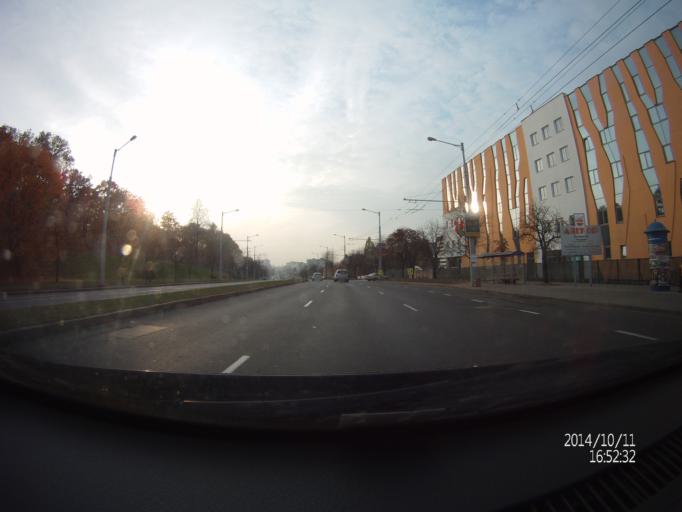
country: BY
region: Minsk
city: Novoye Medvezhino
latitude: 53.9103
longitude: 27.5056
